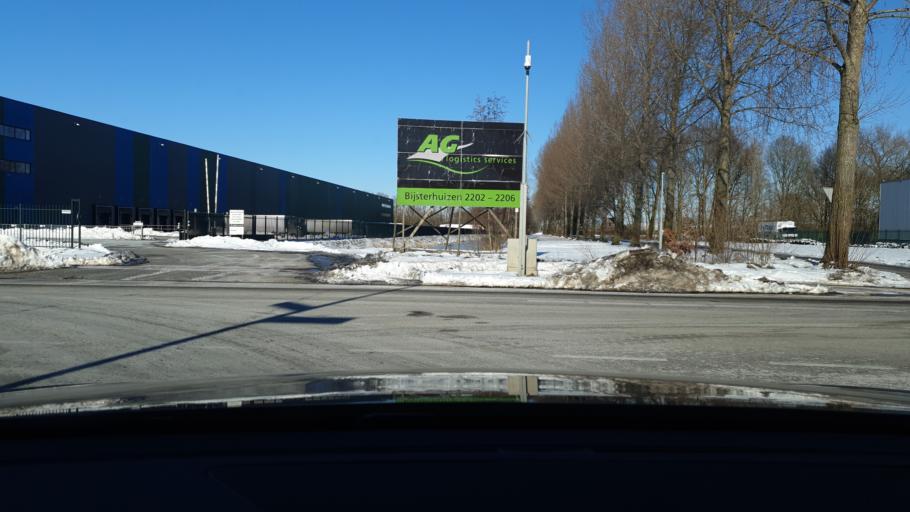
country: NL
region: Gelderland
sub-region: Gemeente Nijmegen
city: Lindenholt
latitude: 51.8288
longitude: 5.7616
